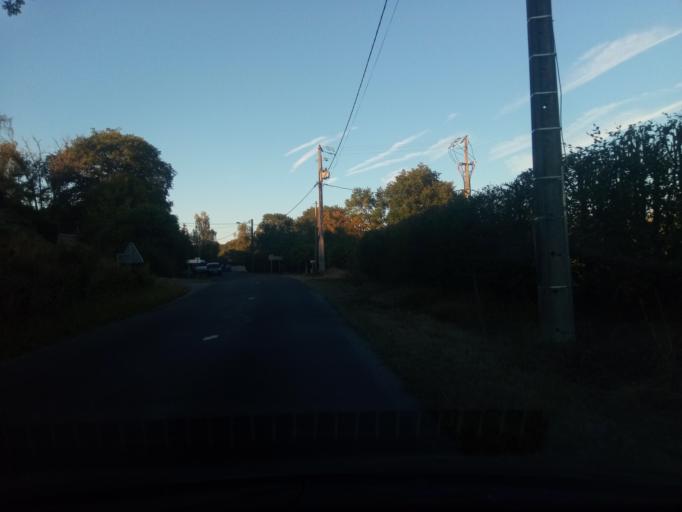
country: FR
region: Poitou-Charentes
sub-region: Departement de la Vienne
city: Montmorillon
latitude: 46.4076
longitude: 0.8795
